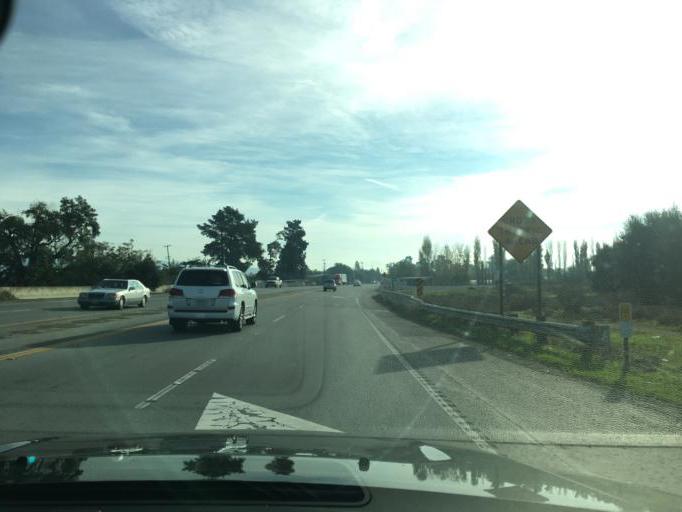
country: US
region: California
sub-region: Santa Clara County
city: Gilroy
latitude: 37.0029
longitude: -121.5354
